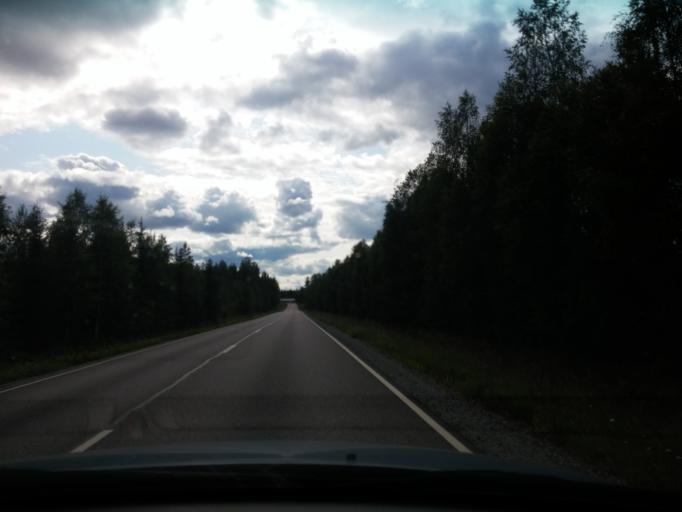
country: FI
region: Central Finland
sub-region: Saarijaervi-Viitasaari
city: Pylkoenmaeki
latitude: 62.6289
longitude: 24.7941
